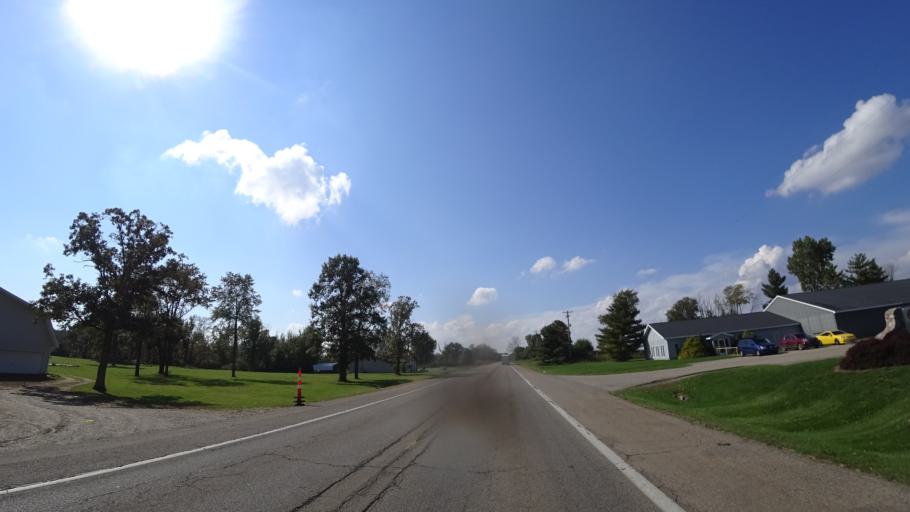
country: US
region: Michigan
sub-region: Calhoun County
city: Homer
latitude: 42.1467
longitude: -84.8303
